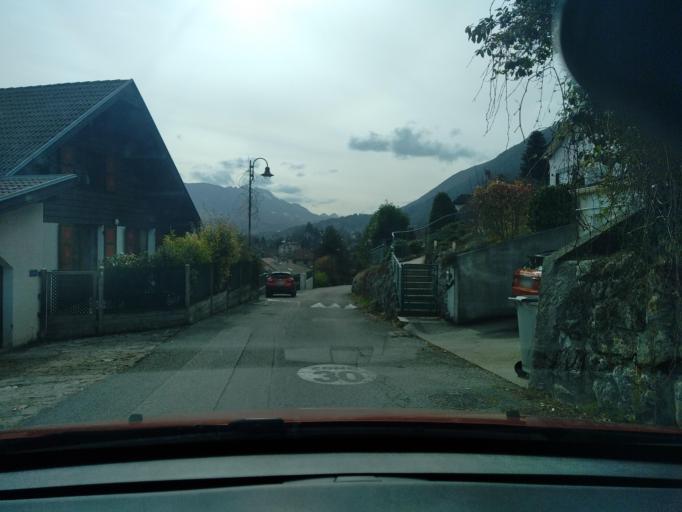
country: FR
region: Rhone-Alpes
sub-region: Departement de la Haute-Savoie
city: Sevrier
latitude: 45.8684
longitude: 6.1393
